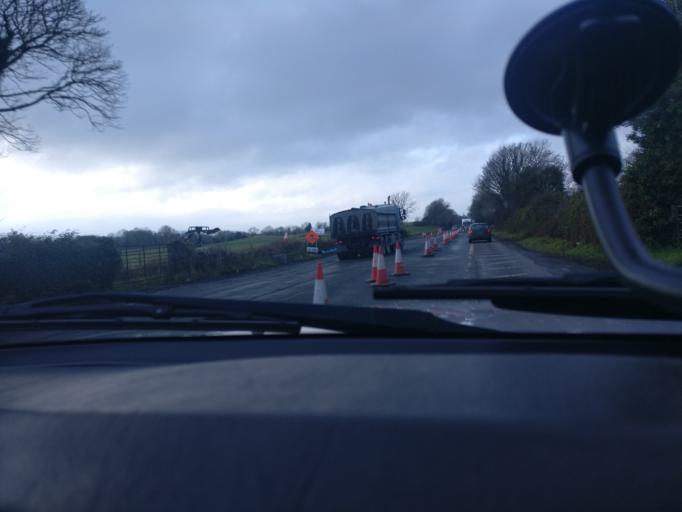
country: IE
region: Connaught
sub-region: County Galway
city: Athenry
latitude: 53.2134
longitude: -8.6851
